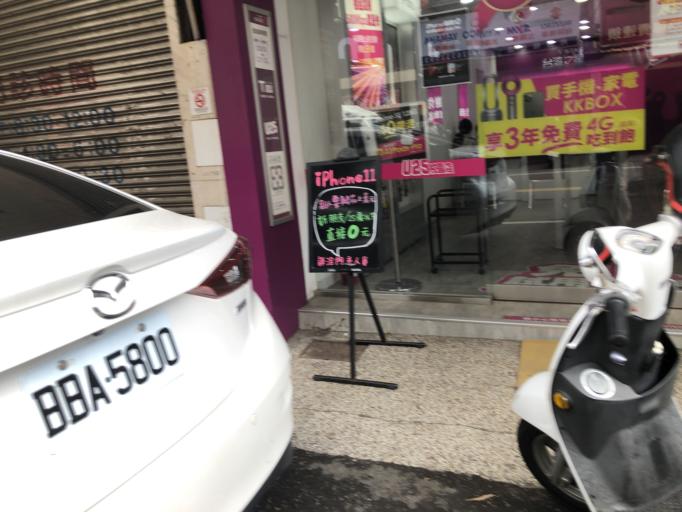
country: TW
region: Taiwan
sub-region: Taichung City
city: Taichung
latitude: 24.1812
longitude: 120.5875
